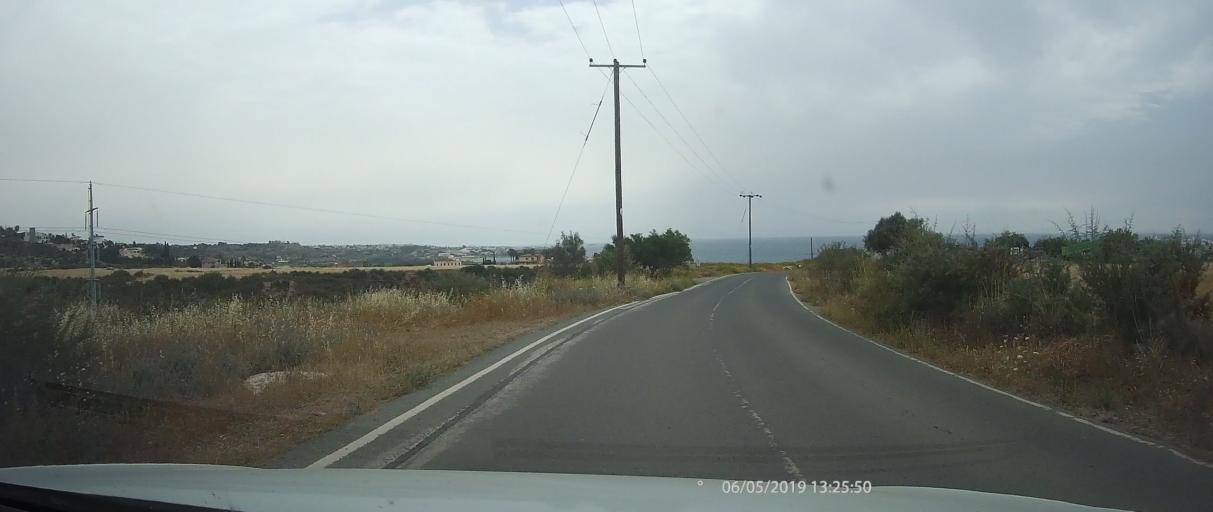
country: CY
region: Pafos
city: Pegeia
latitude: 34.8547
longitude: 32.3863
